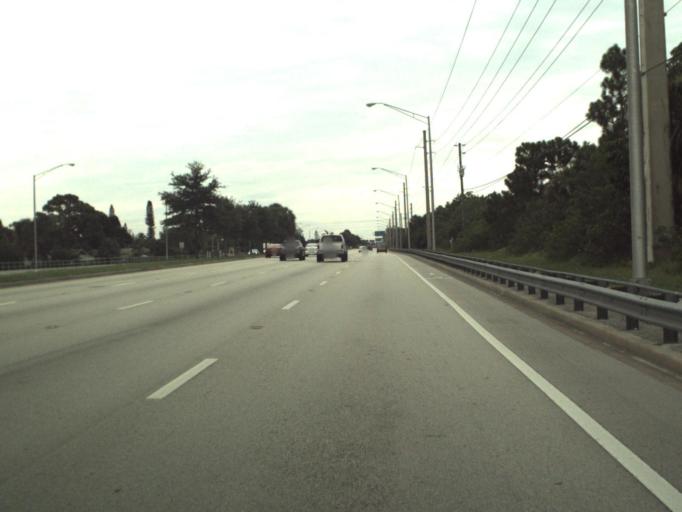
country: US
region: Florida
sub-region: Palm Beach County
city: Lake Belvedere Estates
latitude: 26.6783
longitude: -80.1379
